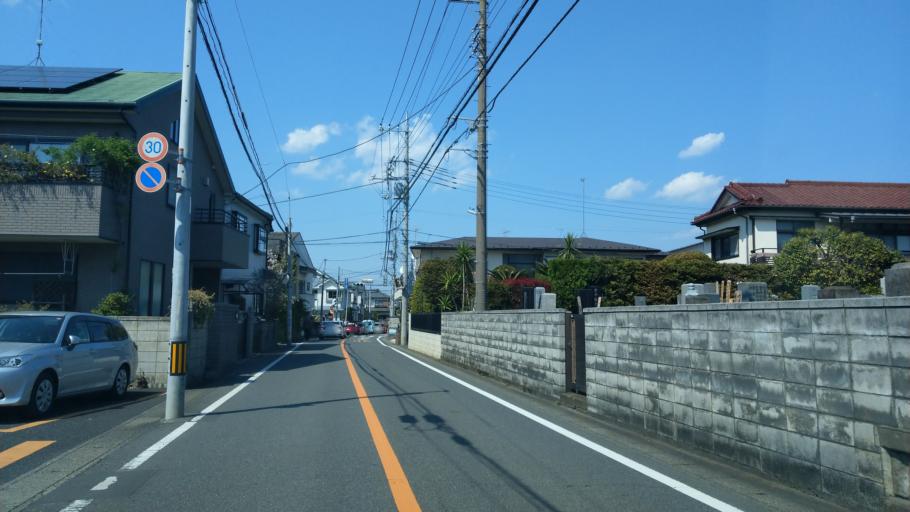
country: JP
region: Saitama
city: Yono
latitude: 35.8613
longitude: 139.6384
